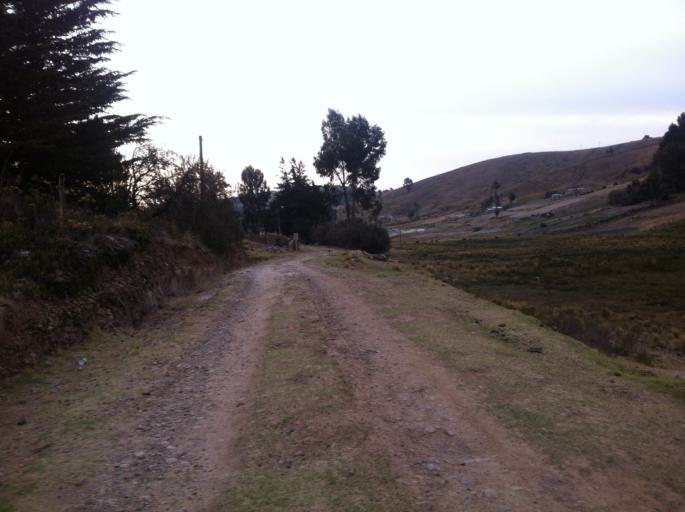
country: PE
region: Puno
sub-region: Yunguyo
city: Yunguyo
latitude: -16.1873
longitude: -69.0824
